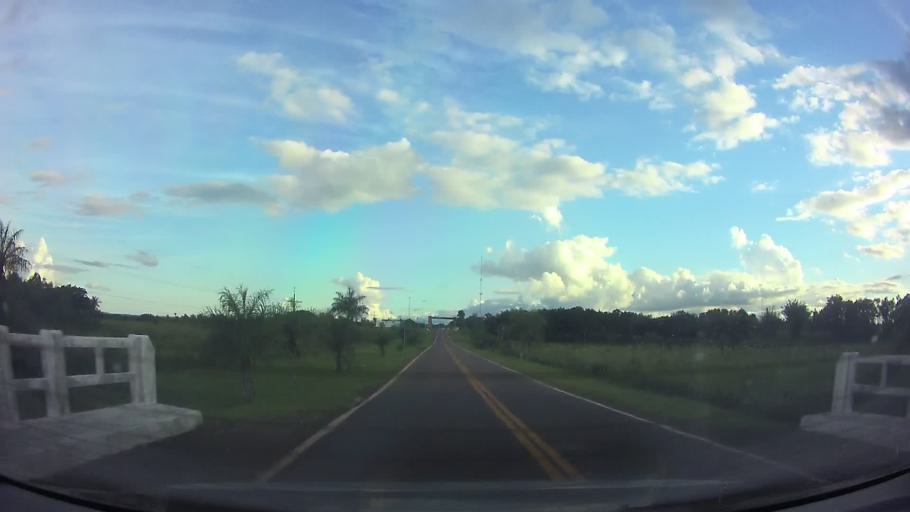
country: PY
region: Paraguari
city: Acahay
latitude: -25.8955
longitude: -57.1183
